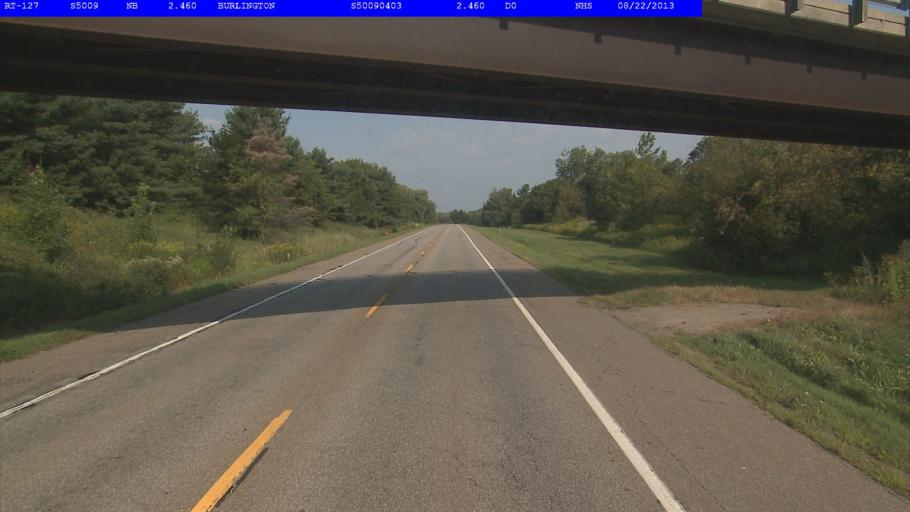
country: US
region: Vermont
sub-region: Chittenden County
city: Burlington
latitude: 44.5175
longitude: -73.2412
